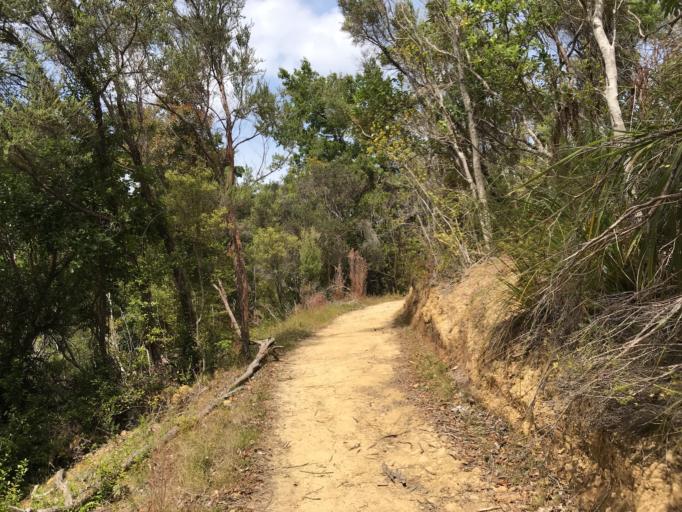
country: NZ
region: Marlborough
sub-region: Marlborough District
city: Picton
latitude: -41.1213
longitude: 174.1907
